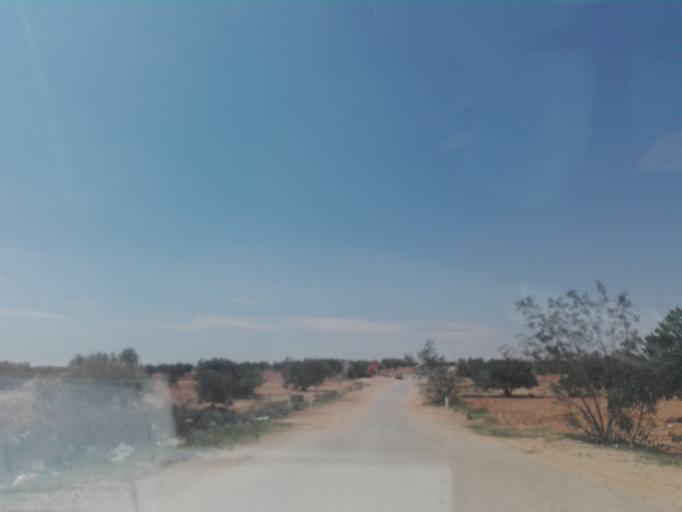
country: TN
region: Safaqis
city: Bi'r `Ali Bin Khalifah
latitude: 34.6174
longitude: 10.3618
